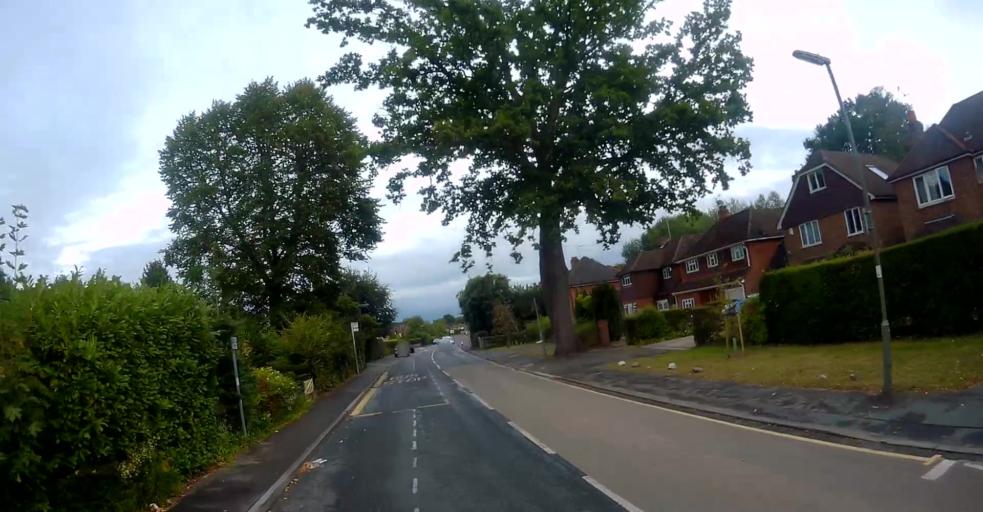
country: GB
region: England
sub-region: Surrey
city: Pirbright
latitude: 51.3047
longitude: -0.6318
